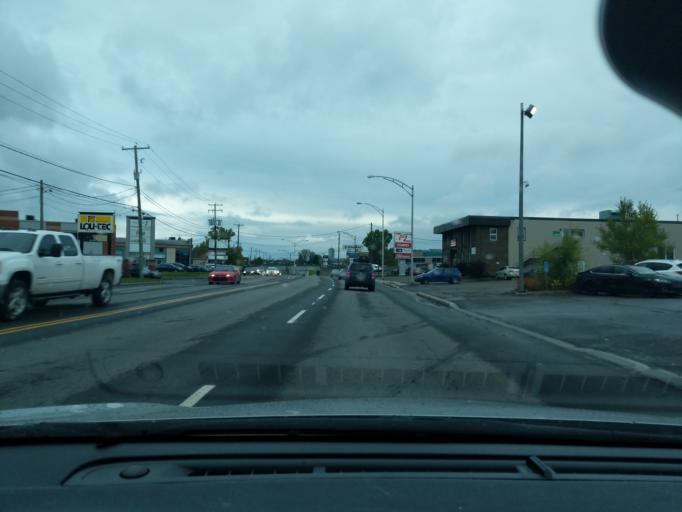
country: CA
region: Quebec
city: Quebec
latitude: 46.8055
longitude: -71.2829
